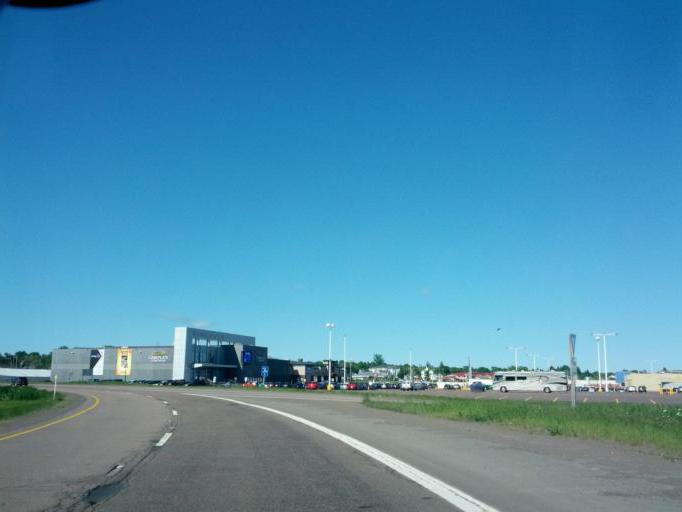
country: CA
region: New Brunswick
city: Moncton
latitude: 46.0963
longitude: -64.7655
